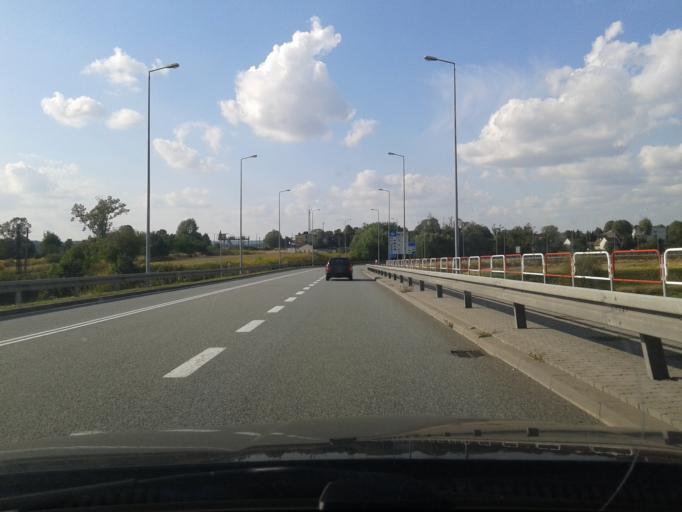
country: PL
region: Silesian Voivodeship
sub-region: Powiat raciborski
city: Chalupki
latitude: 49.9176
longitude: 18.3213
